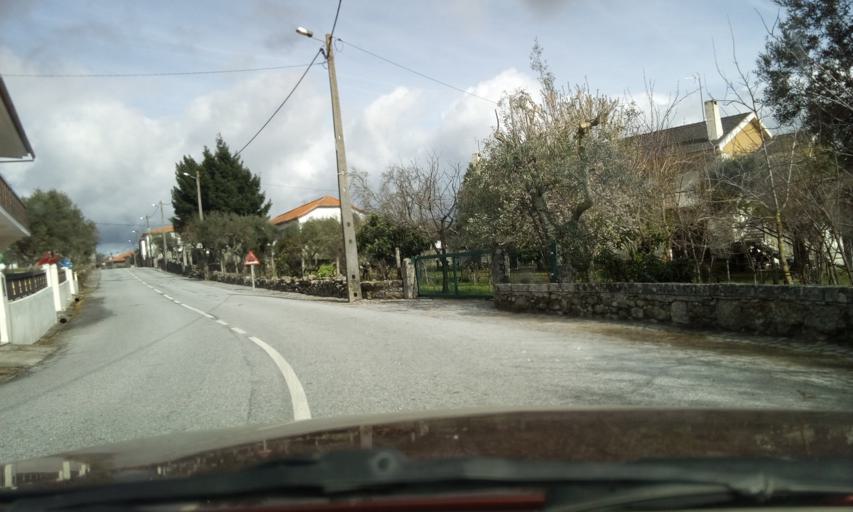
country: PT
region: Guarda
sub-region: Fornos de Algodres
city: Fornos de Algodres
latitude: 40.6486
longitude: -7.5465
